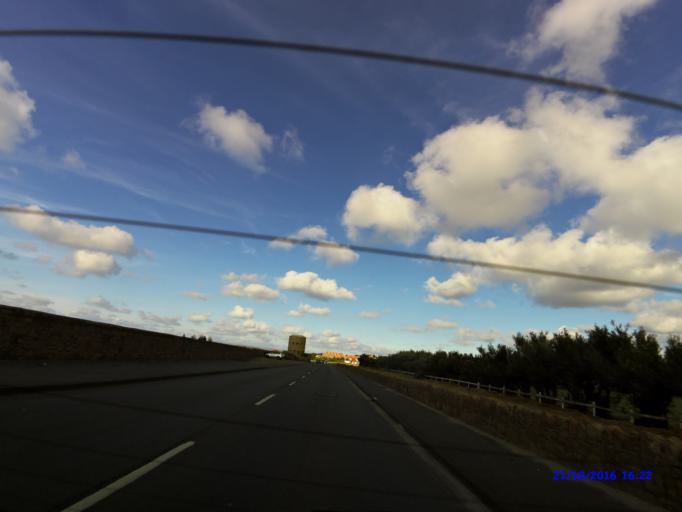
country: GG
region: St Peter Port
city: Saint Peter Port
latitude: 49.4677
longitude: -2.6071
